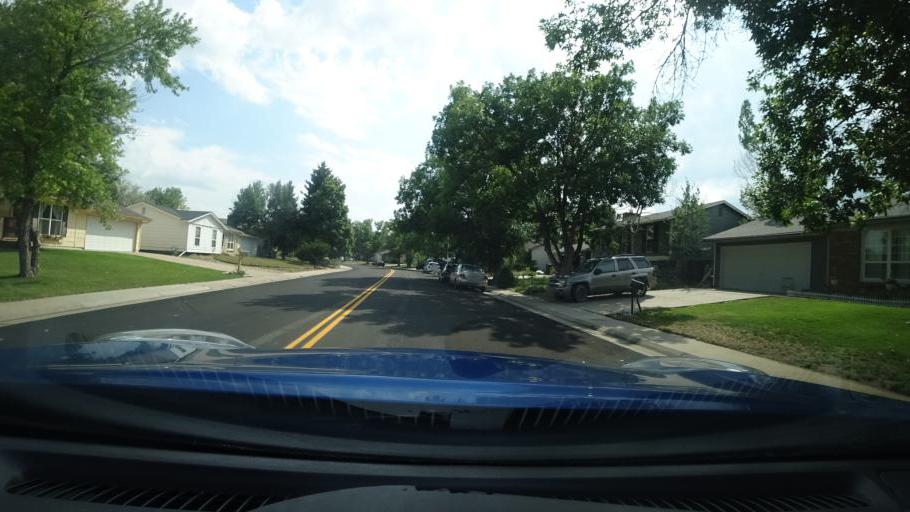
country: US
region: Colorado
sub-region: Adams County
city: Aurora
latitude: 39.6877
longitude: -104.7864
